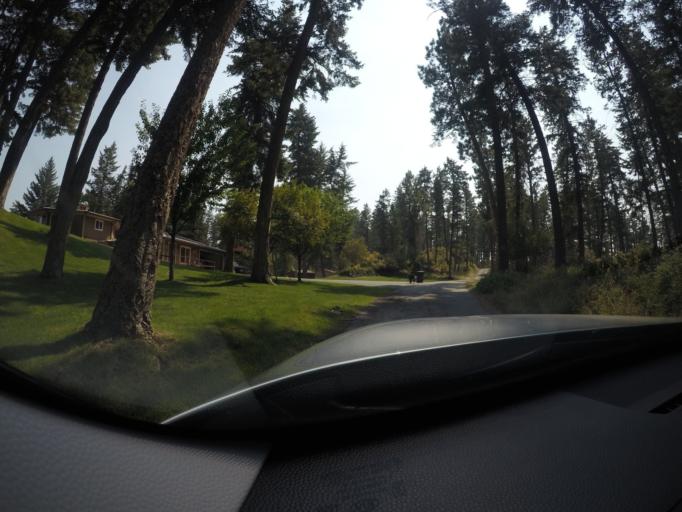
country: US
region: Montana
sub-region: Lake County
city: Polson
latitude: 47.7610
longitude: -114.1436
